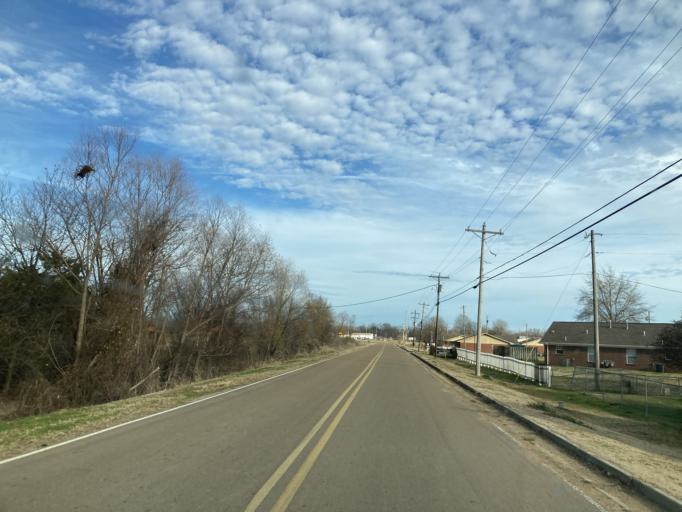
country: US
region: Mississippi
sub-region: Humphreys County
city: Belzoni
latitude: 33.1675
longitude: -90.5019
